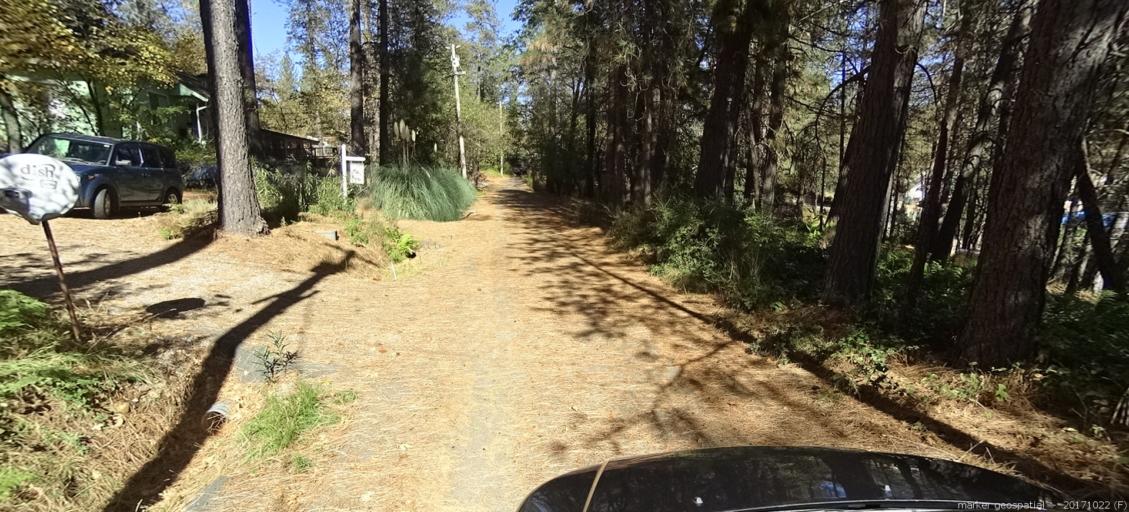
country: US
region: California
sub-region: Shasta County
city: Central Valley (historical)
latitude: 40.8573
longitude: -122.3975
